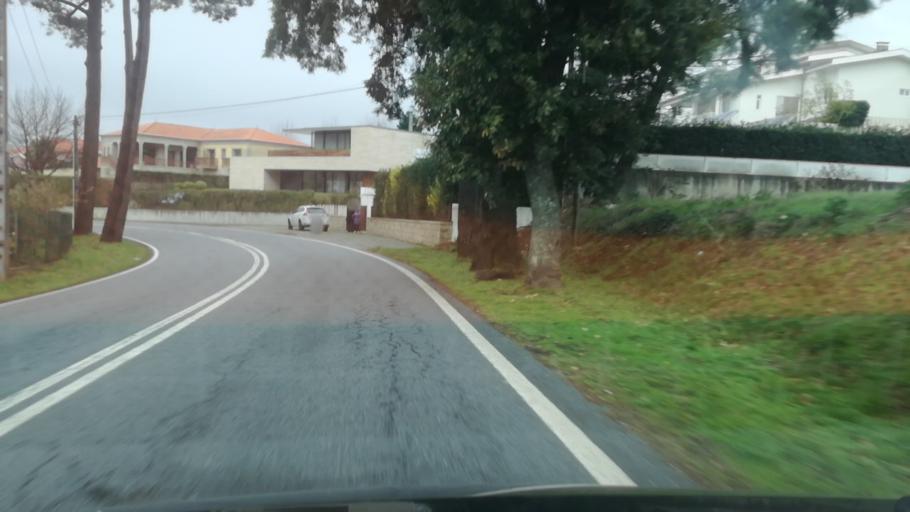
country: PT
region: Braga
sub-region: Braga
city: Braga
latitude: 41.5326
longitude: -8.3977
